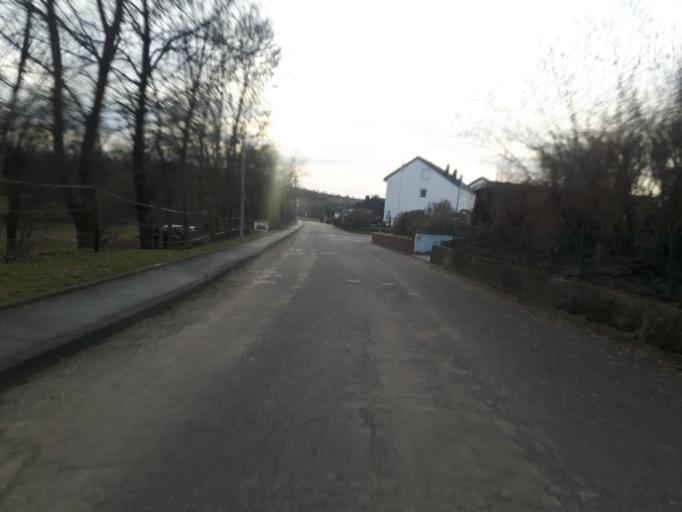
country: DE
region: Baden-Wuerttemberg
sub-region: Regierungsbezirk Stuttgart
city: Neuenstadt am Kocher
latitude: 49.2263
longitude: 9.3736
